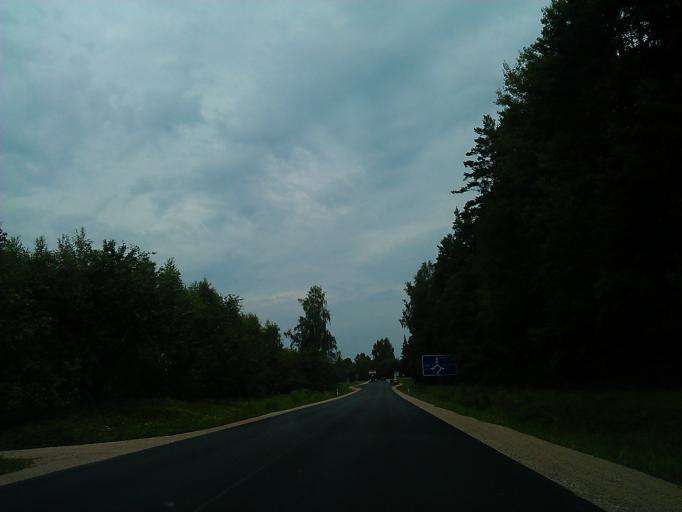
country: LV
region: Valmieras Rajons
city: Valmiera
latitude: 57.5076
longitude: 25.4218
